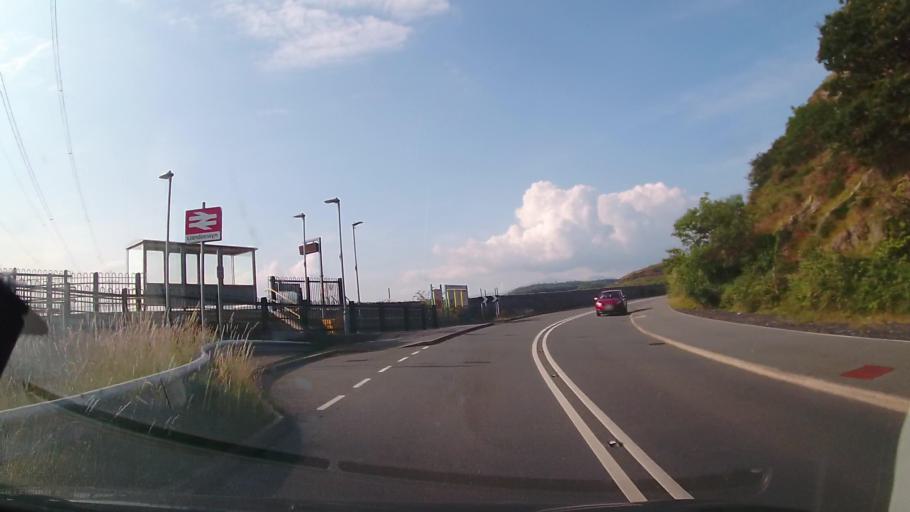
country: GB
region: Wales
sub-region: Gwynedd
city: Penrhyndeudraeth
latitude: 52.9210
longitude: -4.0564
